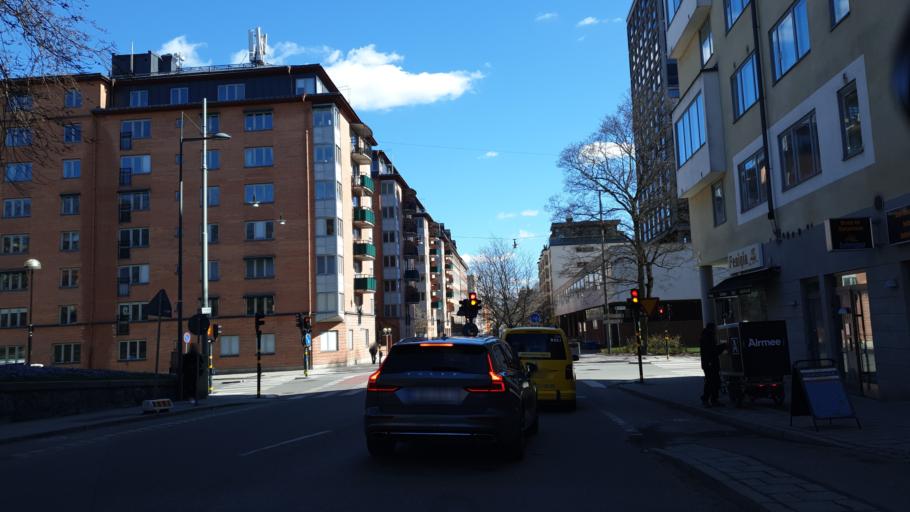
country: SE
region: Stockholm
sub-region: Solna Kommun
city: Solna
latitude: 59.3343
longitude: 18.0243
